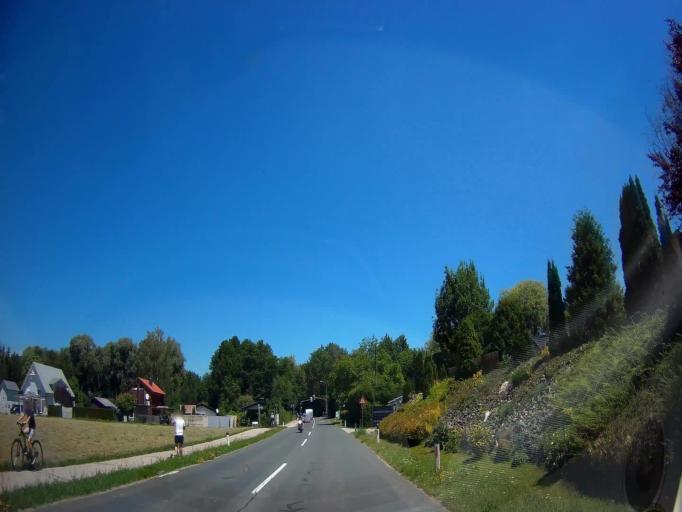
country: AT
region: Carinthia
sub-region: Klagenfurt am Woerthersee
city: Klagenfurt am Woerthersee
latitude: 46.6077
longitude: 14.2576
